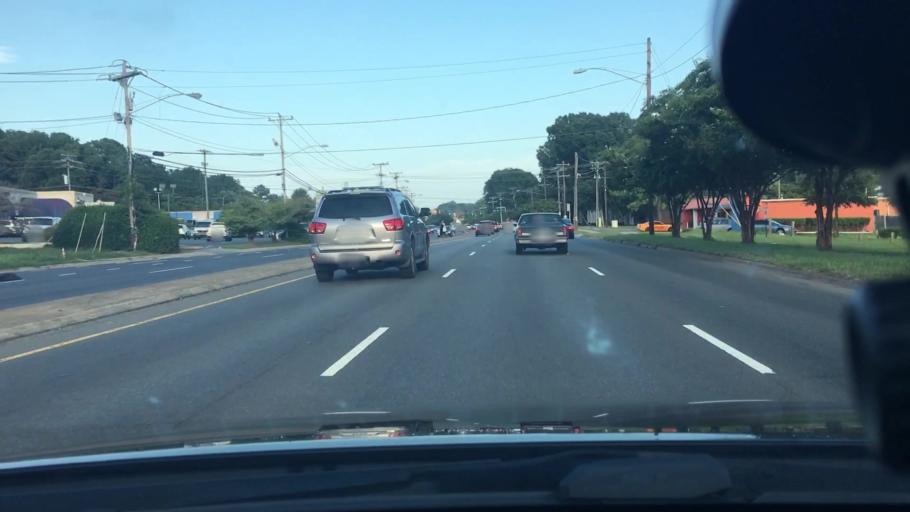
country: US
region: North Carolina
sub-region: Mecklenburg County
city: Matthews
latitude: 35.2035
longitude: -80.7472
